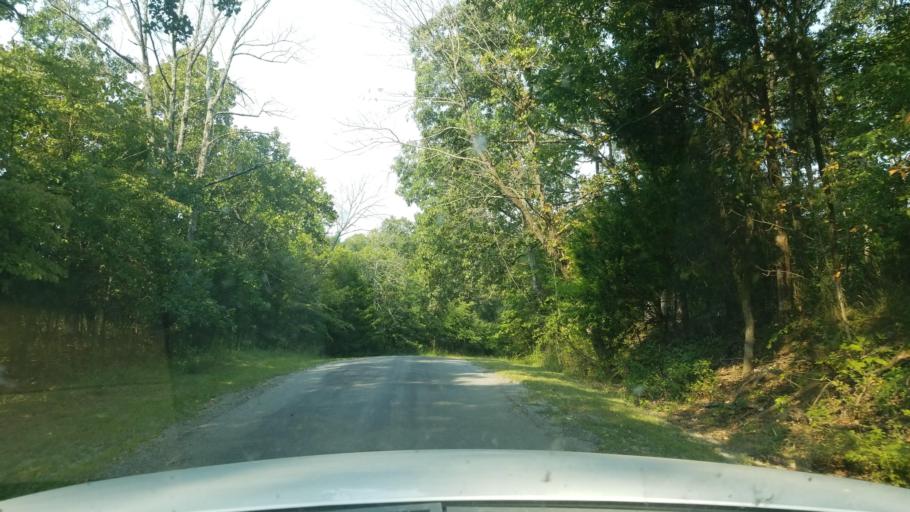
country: US
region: Illinois
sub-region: Saline County
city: Carrier Mills
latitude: 37.7903
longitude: -88.6925
